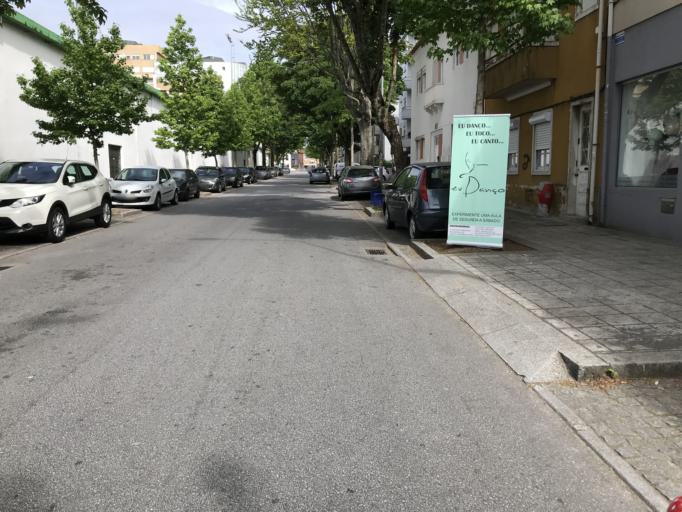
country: PT
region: Porto
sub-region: Matosinhos
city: Senhora da Hora
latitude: 41.1864
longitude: -8.6569
